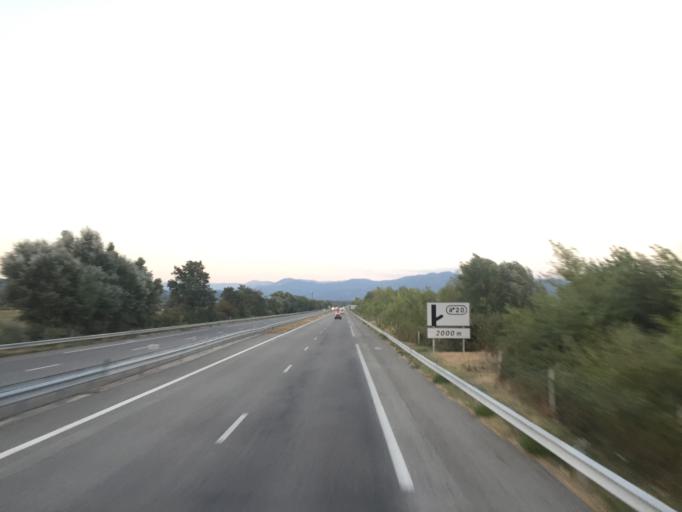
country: FR
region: Provence-Alpes-Cote d'Azur
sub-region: Departement des Alpes-de-Haute-Provence
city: Peyruis
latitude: 44.0245
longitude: 5.9506
